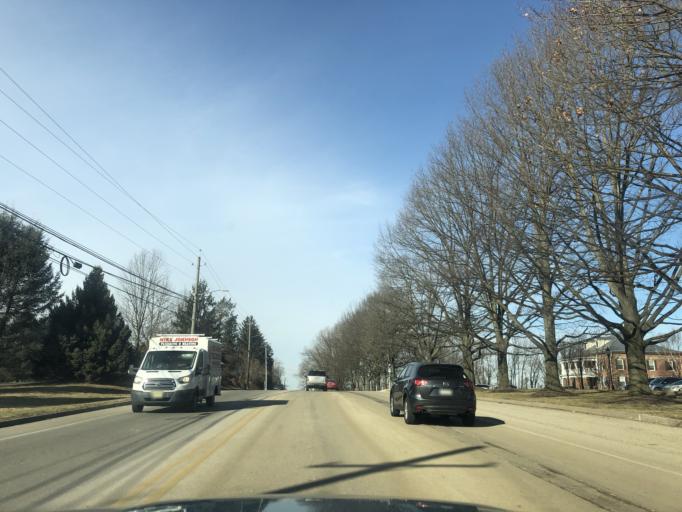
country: US
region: Pennsylvania
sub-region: Montgomery County
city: Plymouth Meeting
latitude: 40.0772
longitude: -75.2484
